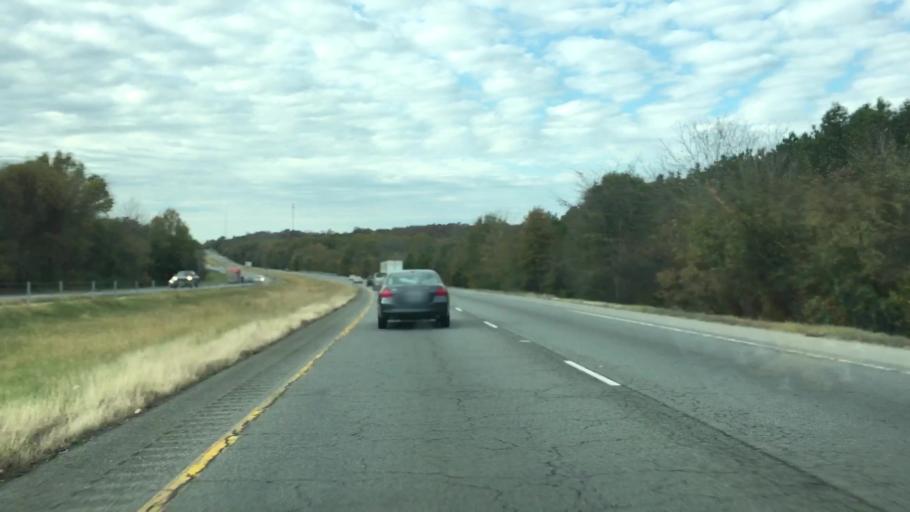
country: US
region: Arkansas
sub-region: Faulkner County
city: Conway
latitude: 35.1370
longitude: -92.5210
